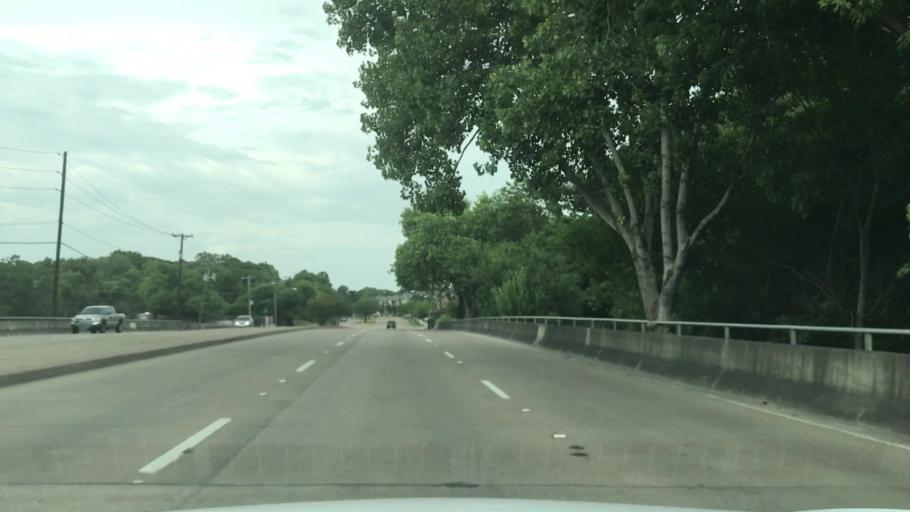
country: US
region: Texas
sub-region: Dallas County
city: Highland Park
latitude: 32.8673
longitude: -96.7399
